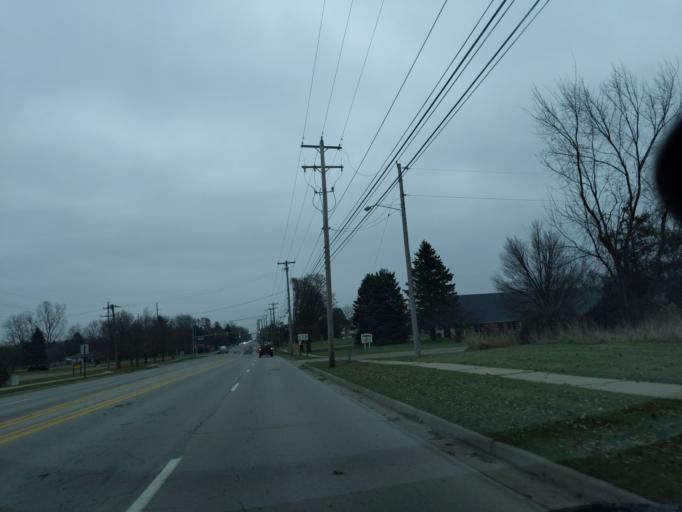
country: US
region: Michigan
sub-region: Eaton County
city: Waverly
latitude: 42.7266
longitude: -84.6251
